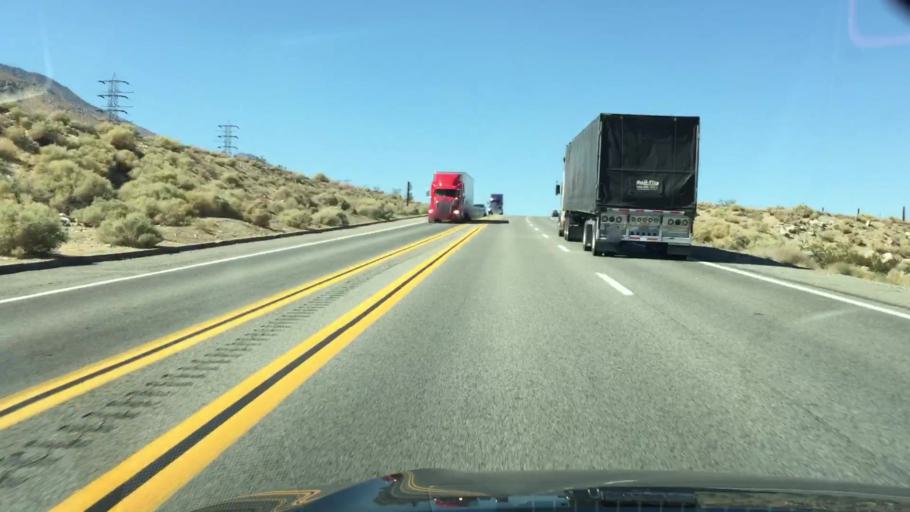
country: US
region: California
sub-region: Inyo County
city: Lone Pine
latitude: 36.3509
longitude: -118.0254
